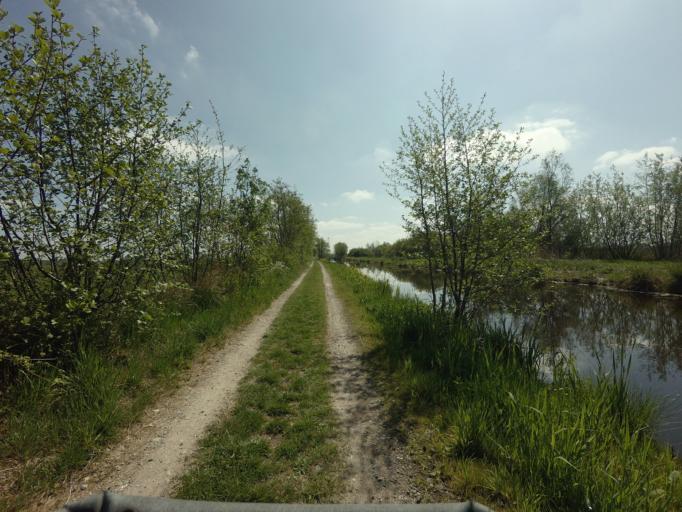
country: NL
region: South Holland
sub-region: Gemeente Gouda
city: Gouda
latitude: 51.9877
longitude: 4.7185
